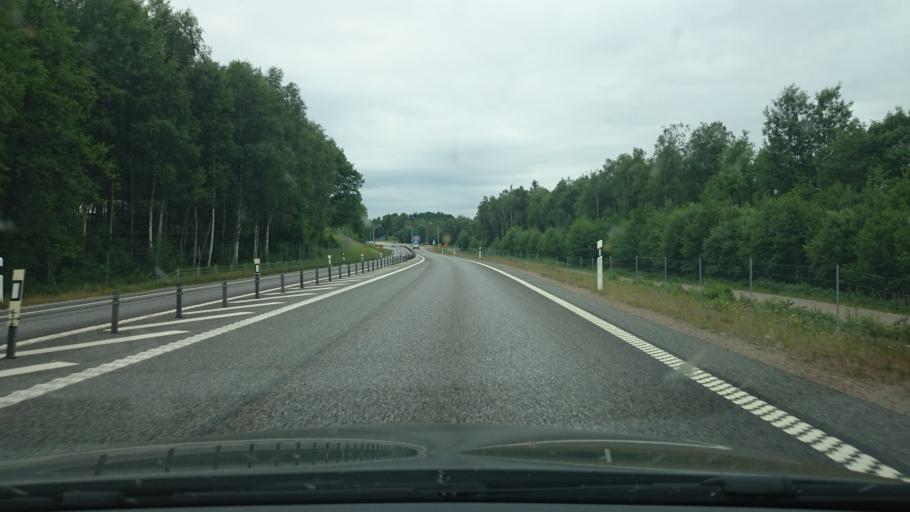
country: SE
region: Halland
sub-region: Hylte Kommun
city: Hyltebruk
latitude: 56.9846
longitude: 13.2131
